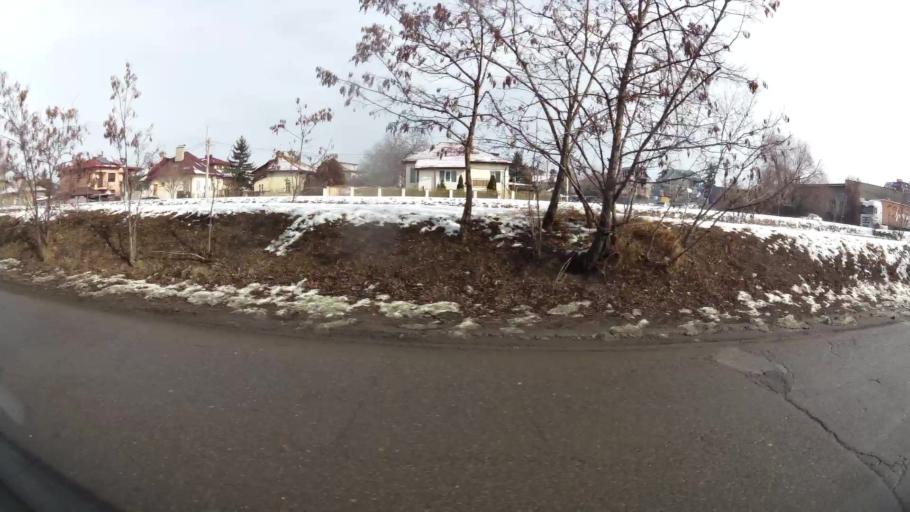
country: BG
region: Sofia-Capital
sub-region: Stolichna Obshtina
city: Sofia
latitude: 42.7039
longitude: 23.3722
